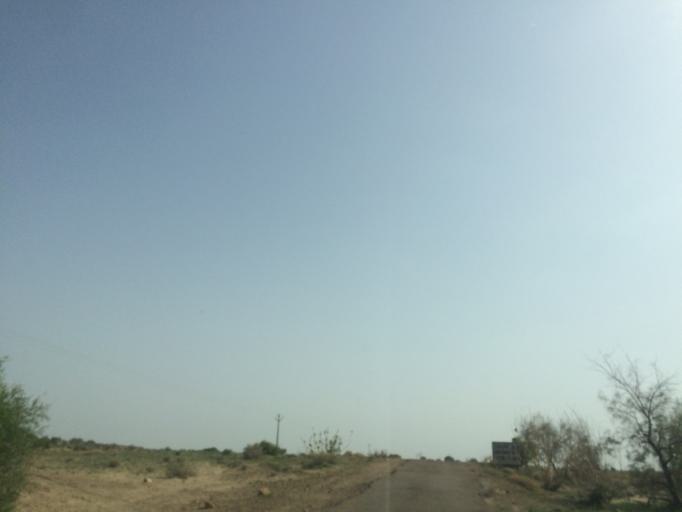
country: IN
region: Rajasthan
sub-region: Jaisalmer
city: Jaisalmer
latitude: 26.8733
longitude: 70.7767
